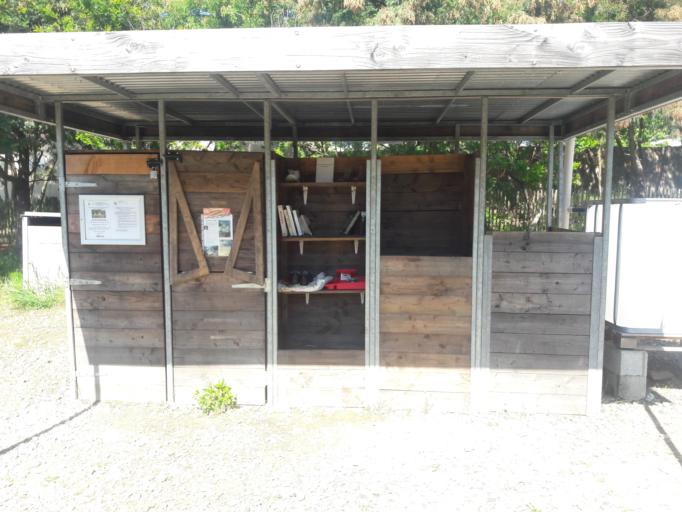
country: FR
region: Pays de la Loire
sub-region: Departement de la Loire-Atlantique
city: Sainte-Luce-sur-Loire
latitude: 47.2435
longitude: -1.5168
